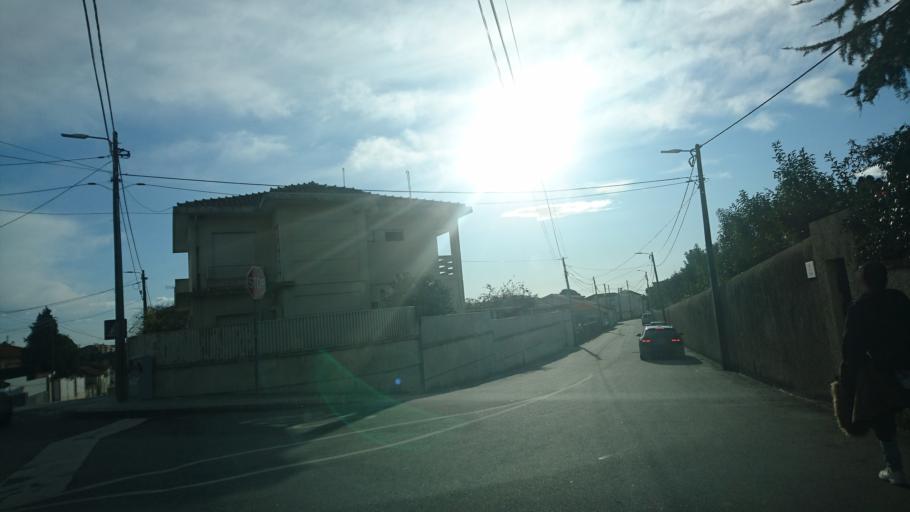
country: PT
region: Aveiro
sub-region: Santa Maria da Feira
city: Pacos de Brandao
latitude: 40.9692
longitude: -8.5912
